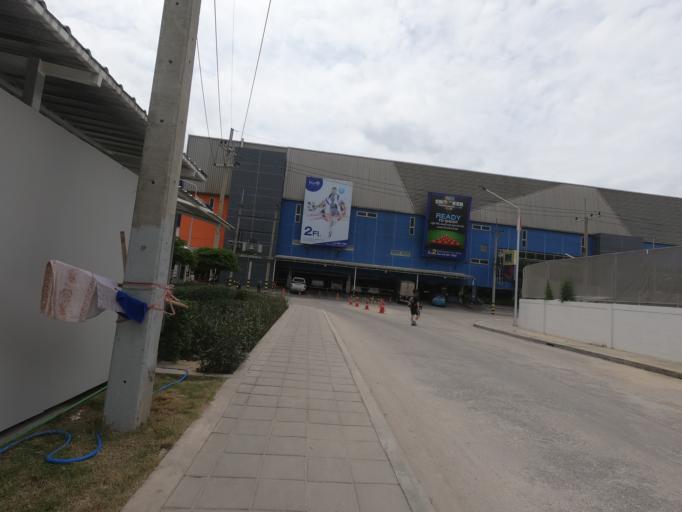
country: TH
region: Bangkok
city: Sai Mai
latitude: 13.9389
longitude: 100.6523
